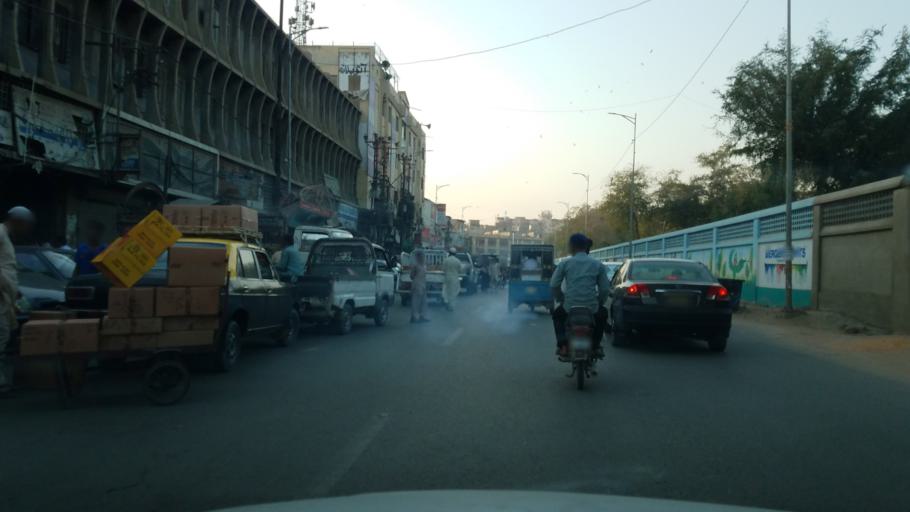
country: PK
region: Sindh
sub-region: Karachi District
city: Karachi
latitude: 24.8741
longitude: 67.0222
